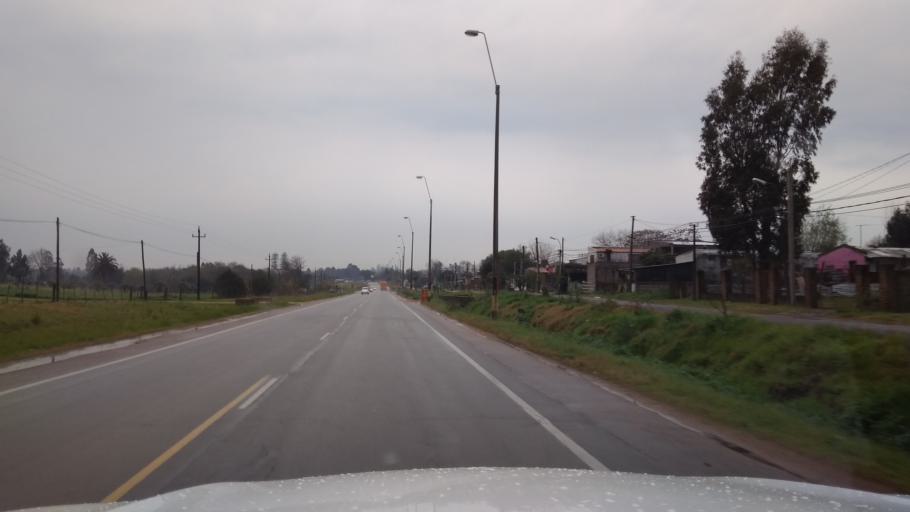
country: UY
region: Canelones
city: Toledo
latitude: -34.7593
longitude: -56.1142
